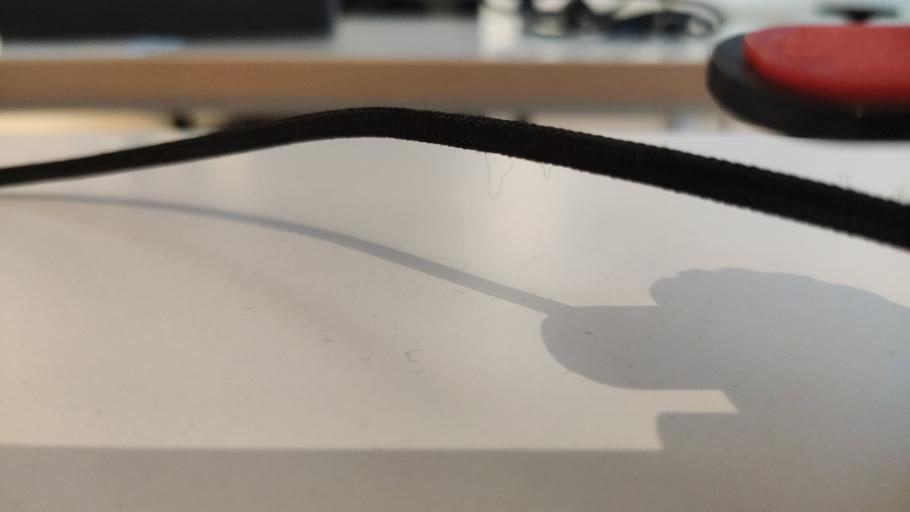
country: RU
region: Moskovskaya
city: Novopetrovskoye
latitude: 55.8576
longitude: 36.3788
